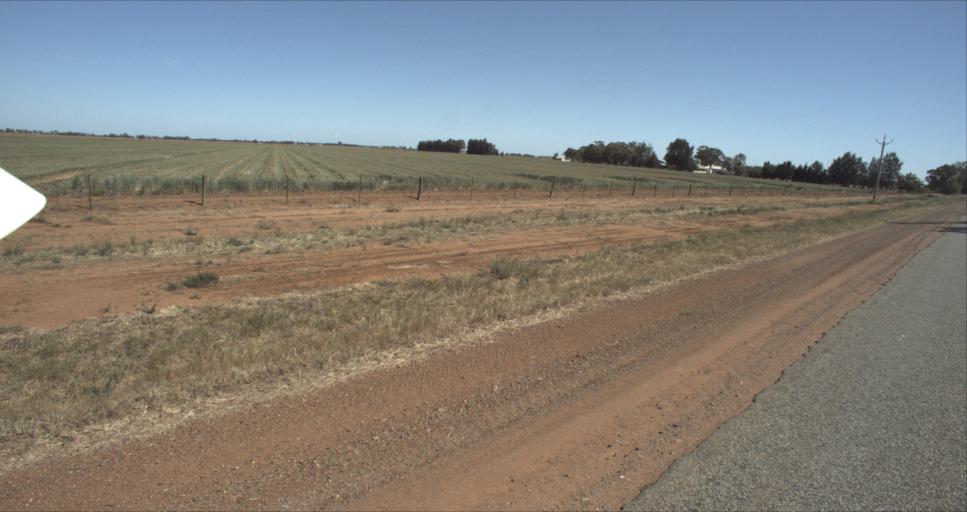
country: AU
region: New South Wales
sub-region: Leeton
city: Leeton
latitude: -34.5472
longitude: 146.3153
